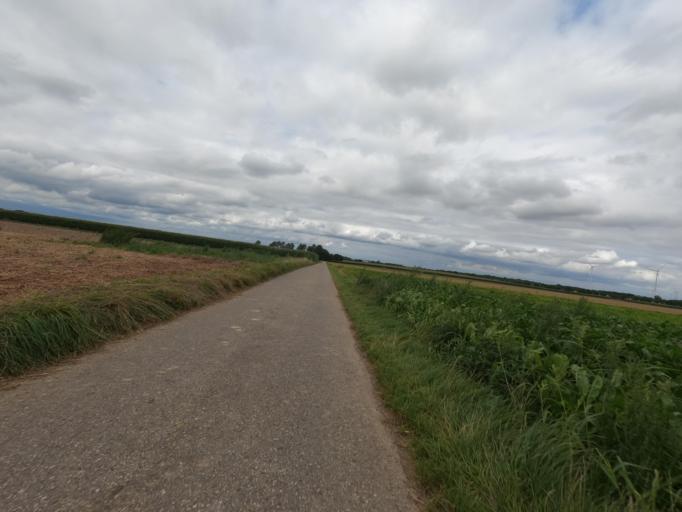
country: DE
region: North Rhine-Westphalia
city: Baesweiler
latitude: 50.9626
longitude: 6.1873
